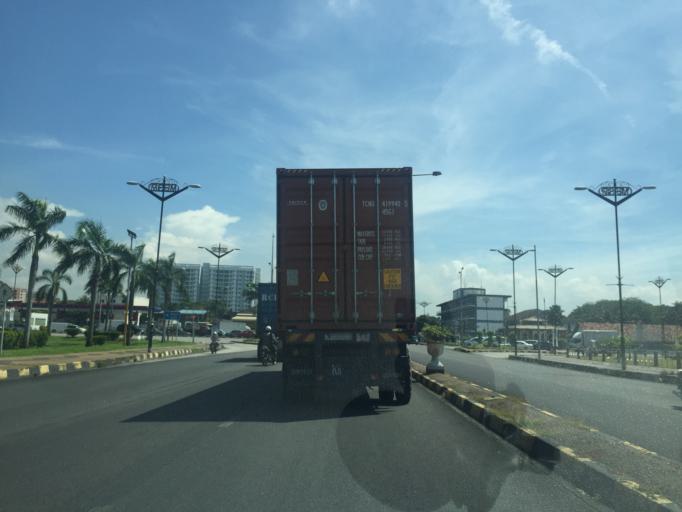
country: MY
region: Penang
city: Butterworth
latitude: 5.4074
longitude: 100.3691
